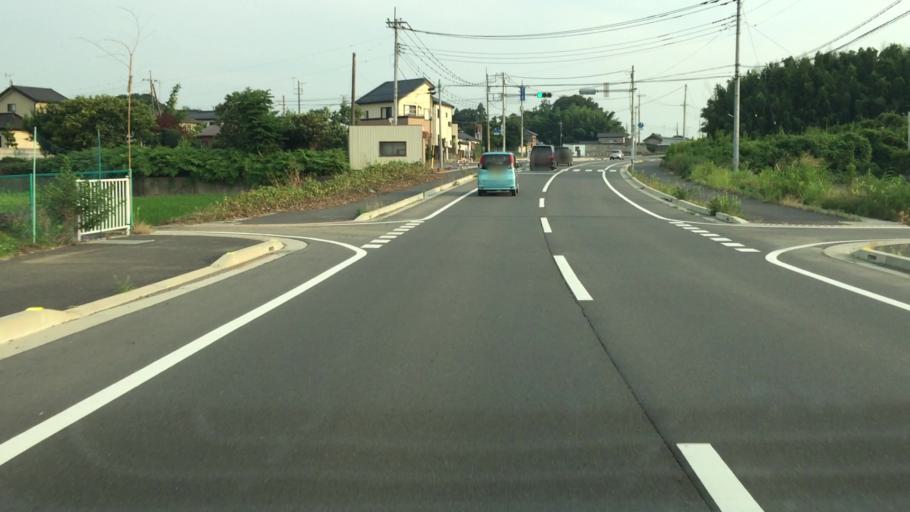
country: JP
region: Gunma
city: Tatebayashi
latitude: 36.2289
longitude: 139.5897
